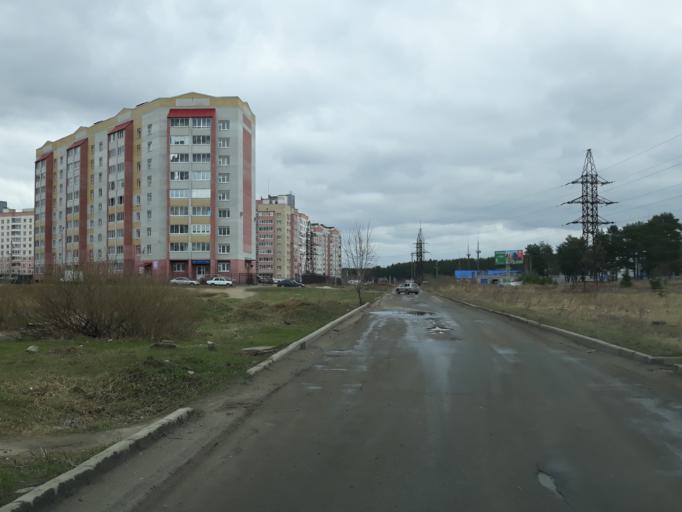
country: RU
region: Jaroslavl
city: Yaroslavl
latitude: 57.6479
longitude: 39.9651
